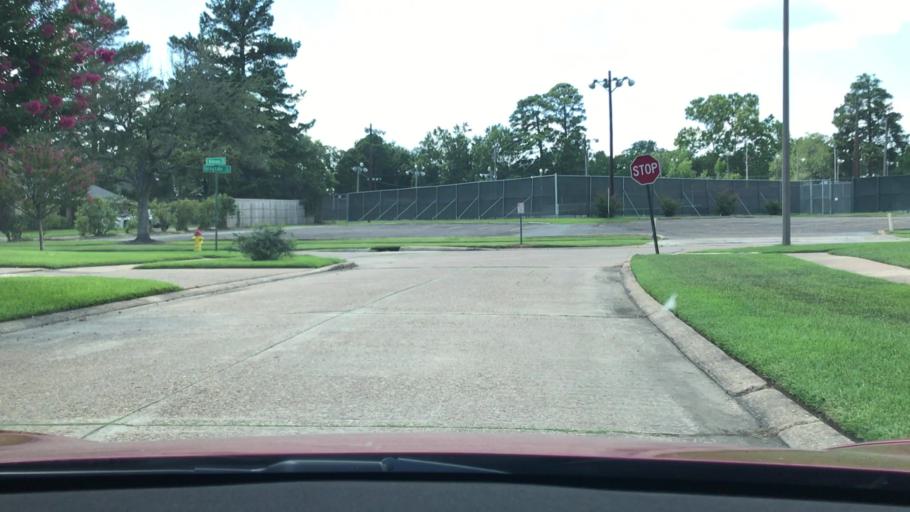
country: US
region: Louisiana
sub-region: Bossier Parish
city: Bossier City
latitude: 32.4312
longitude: -93.7367
